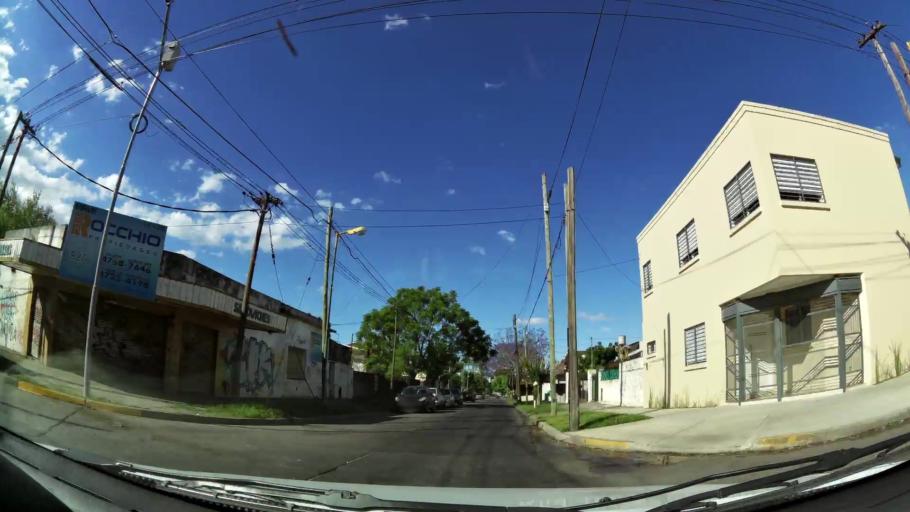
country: AR
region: Buenos Aires
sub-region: Partido de General San Martin
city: General San Martin
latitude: -34.5377
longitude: -58.5651
